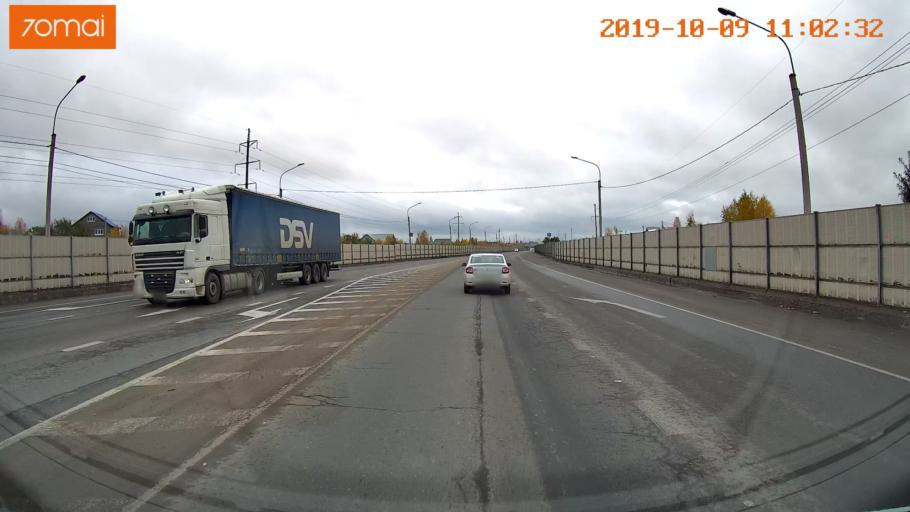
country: RU
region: Vologda
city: Vologda
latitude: 59.2312
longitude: 39.7746
